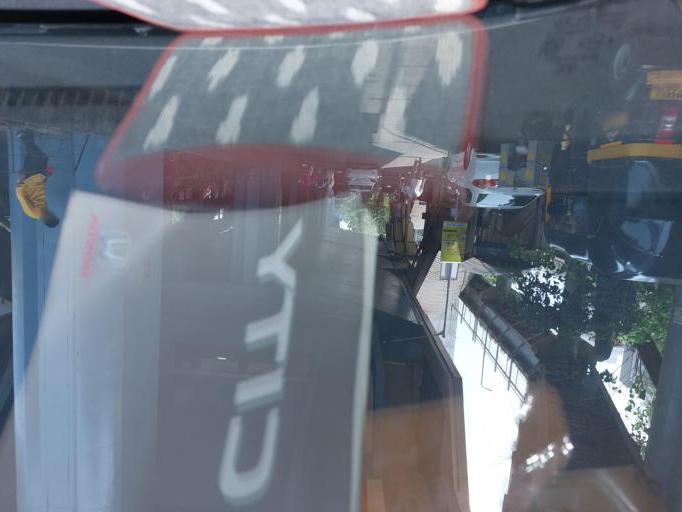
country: IN
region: Maharashtra
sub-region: Mumbai Suburban
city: Mumbai
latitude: 19.0615
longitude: 72.8977
